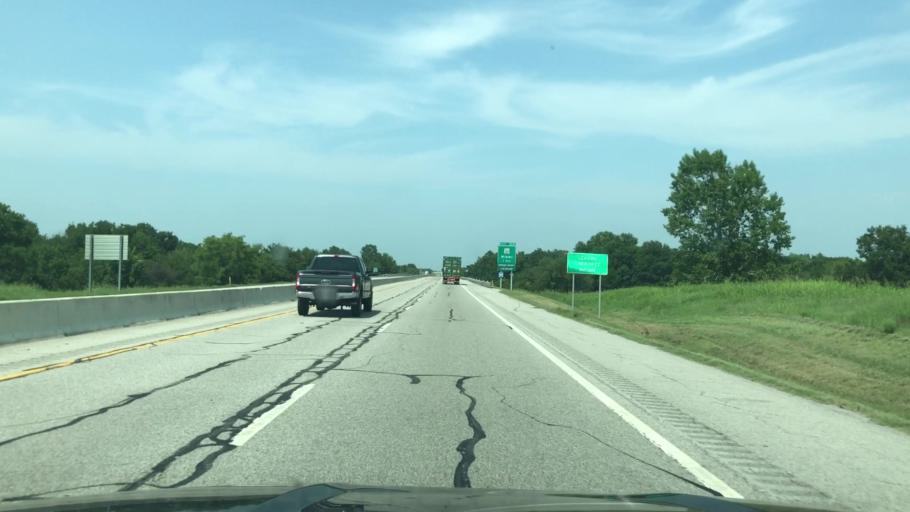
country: US
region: Oklahoma
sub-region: Ottawa County
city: Miami
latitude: 36.8493
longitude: -94.8572
